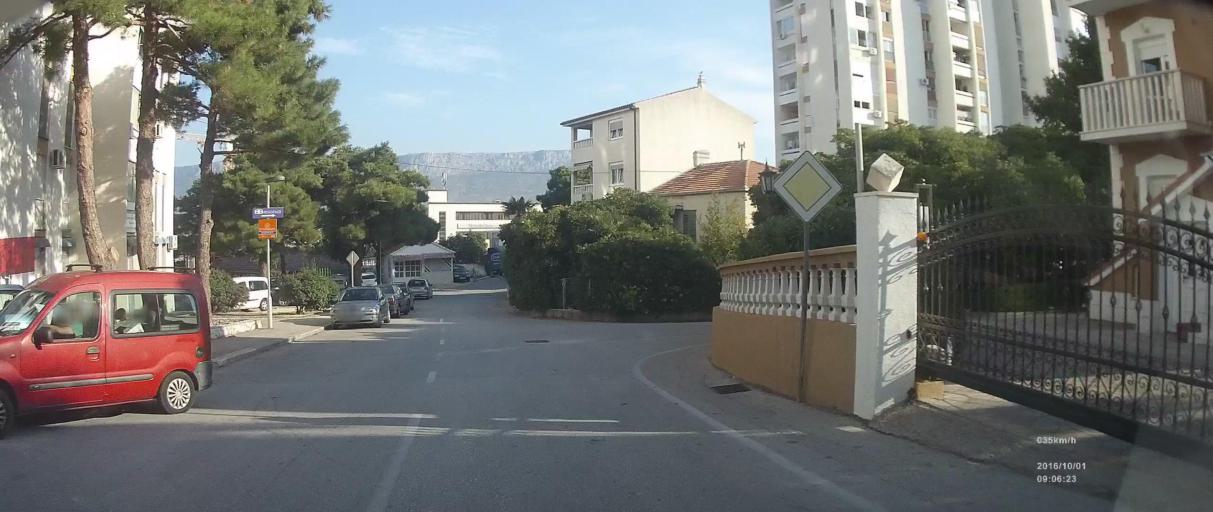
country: HR
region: Splitsko-Dalmatinska
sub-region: Grad Split
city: Split
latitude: 43.5190
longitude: 16.4513
